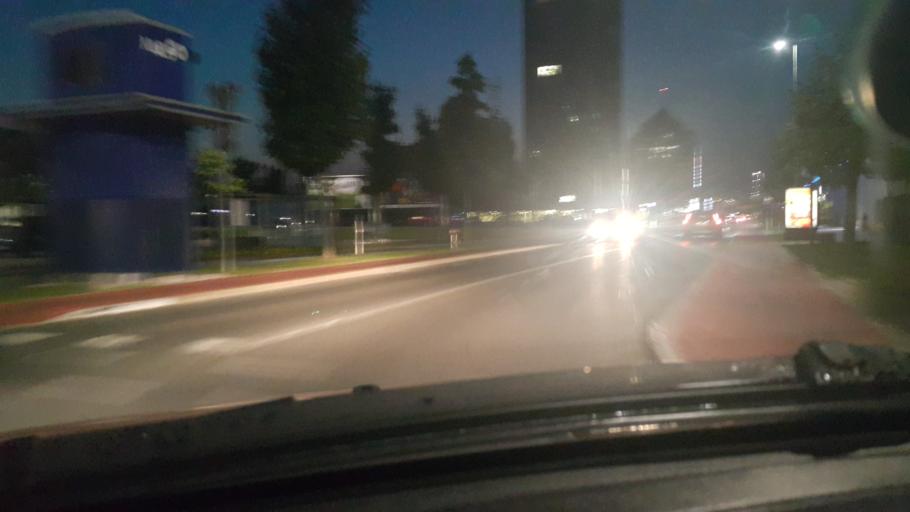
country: SI
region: Ljubljana
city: Ljubljana
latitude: 46.0650
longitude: 14.5432
